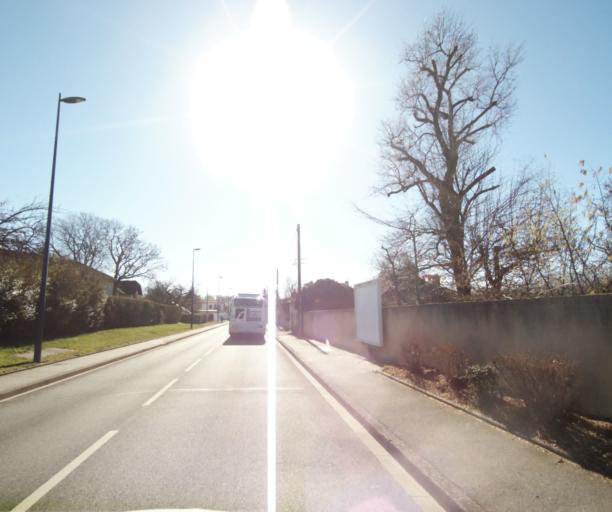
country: FR
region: Lorraine
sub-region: Departement de Meurthe-et-Moselle
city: Heillecourt
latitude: 48.6621
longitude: 6.2072
